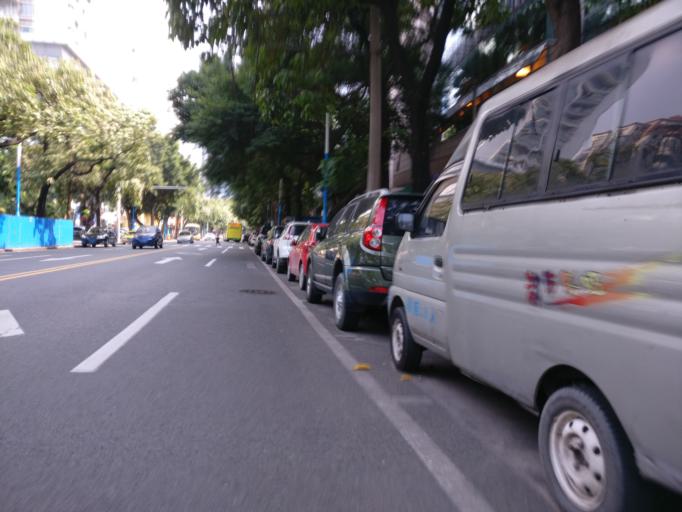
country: CN
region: Guangdong
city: Guangzhou
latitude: 23.1280
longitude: 113.2732
